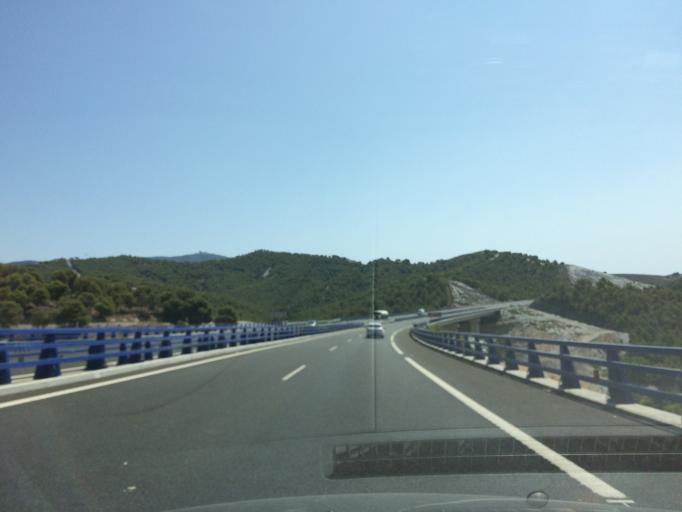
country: ES
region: Andalusia
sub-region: Provincia de Granada
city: Motril
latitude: 36.7717
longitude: -3.4887
